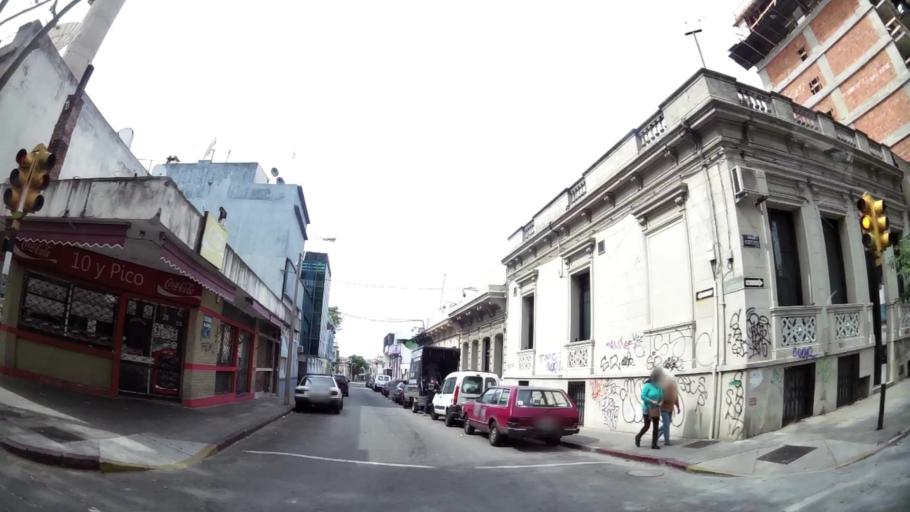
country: UY
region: Montevideo
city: Montevideo
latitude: -34.9081
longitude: -56.1810
